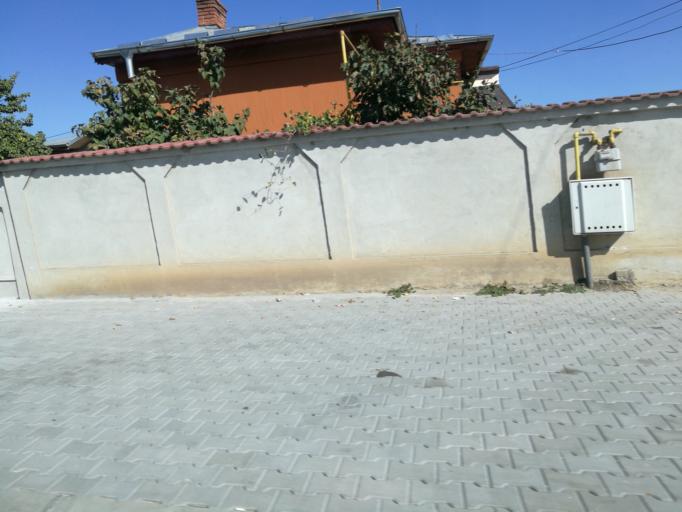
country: RO
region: Ilfov
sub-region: Comuna Dragomiresti-Vale
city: Dragomiresti-Deal
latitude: 44.4603
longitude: 25.9454
